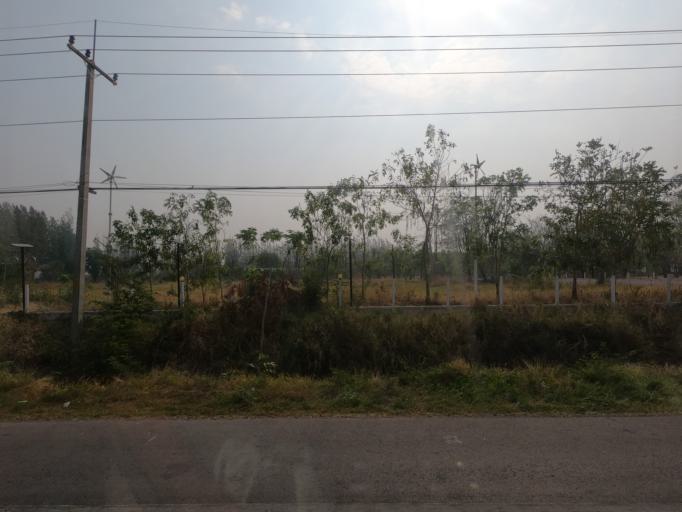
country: TH
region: Khon Kaen
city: Ban Phai
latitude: 16.0857
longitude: 102.7273
